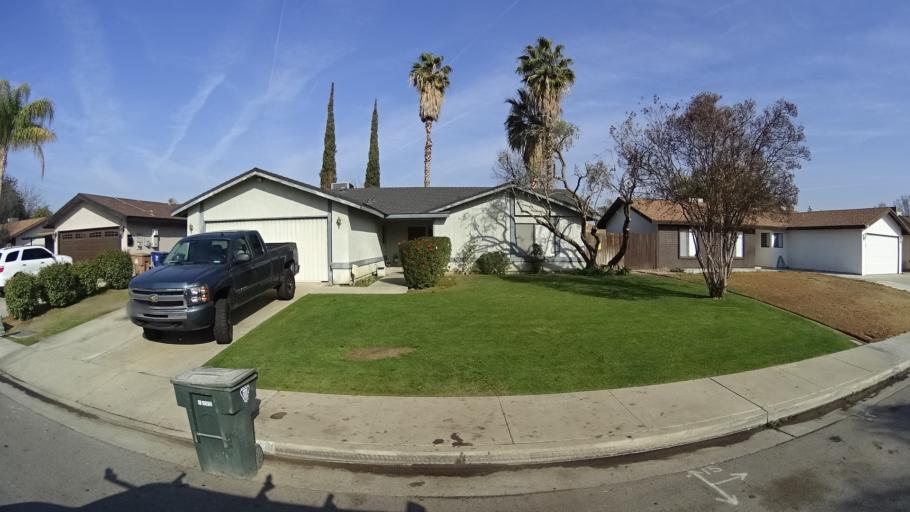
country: US
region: California
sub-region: Kern County
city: Bakersfield
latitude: 35.3233
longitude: -119.0425
